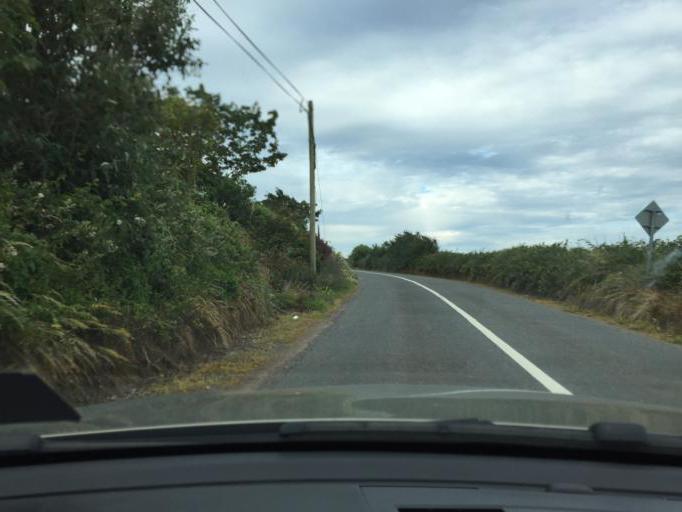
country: IE
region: Munster
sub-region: County Cork
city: Youghal
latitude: 51.9783
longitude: -7.7165
